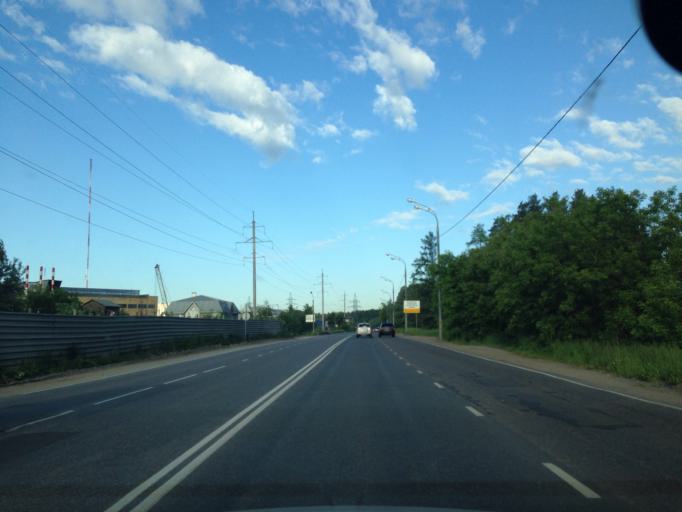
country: RU
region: Moscow
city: Vostochnyy
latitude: 55.8042
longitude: 37.9073
